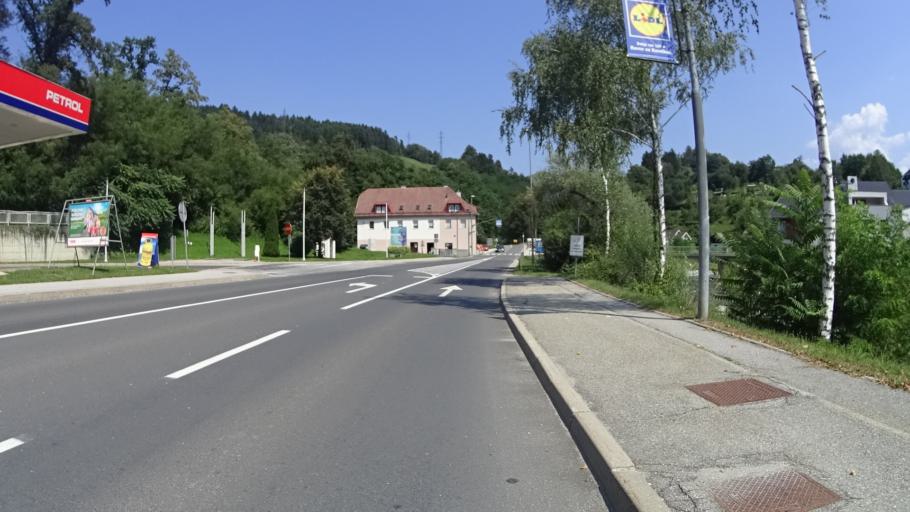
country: SI
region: Ravne na Koroskem
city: Ravne na Koroskem
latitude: 46.5470
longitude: 14.9650
